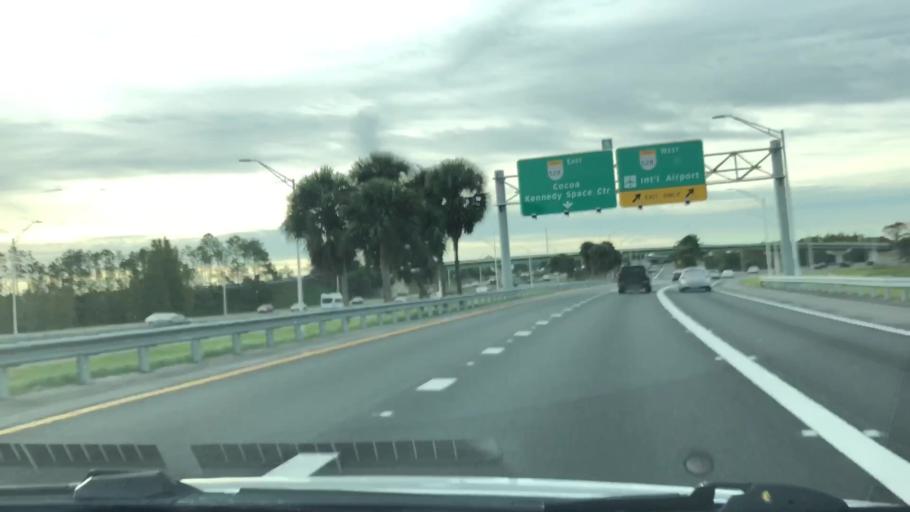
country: US
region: Florida
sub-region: Orange County
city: Conway
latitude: 28.4558
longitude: -81.2311
